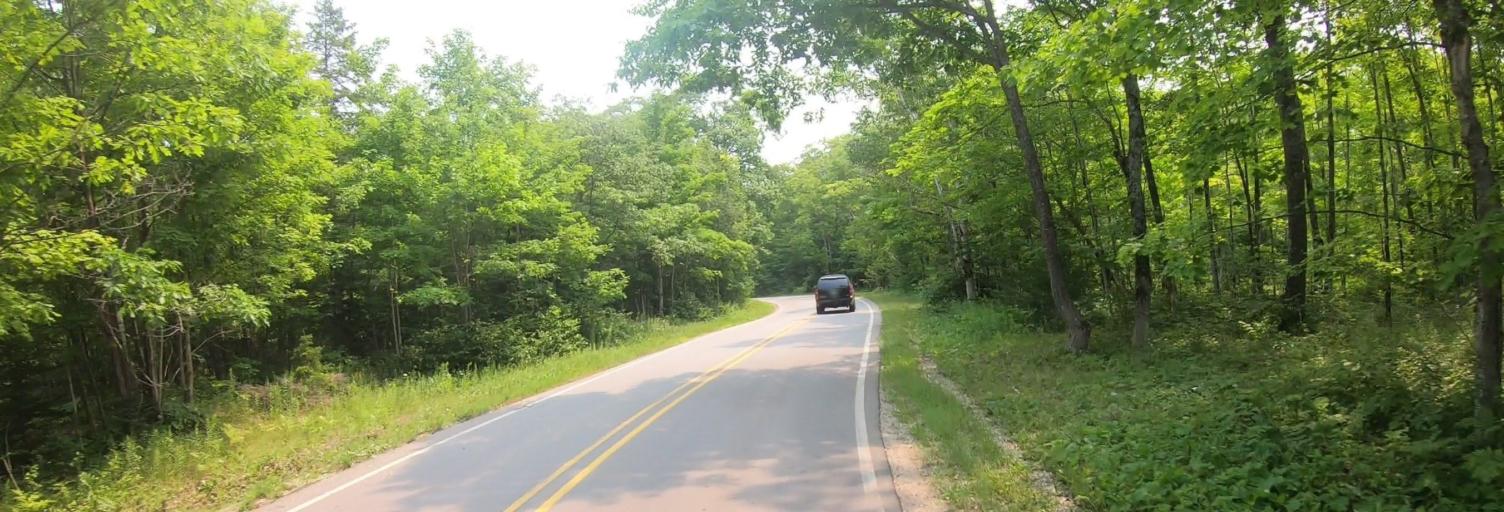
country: CA
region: Ontario
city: Thessalon
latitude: 45.9443
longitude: -83.5868
